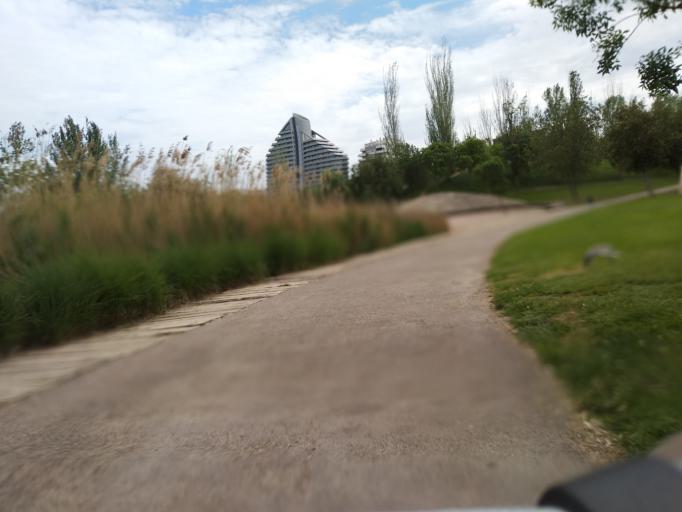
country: ES
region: Valencia
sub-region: Provincia de Valencia
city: Mislata
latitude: 39.4763
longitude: -0.4091
